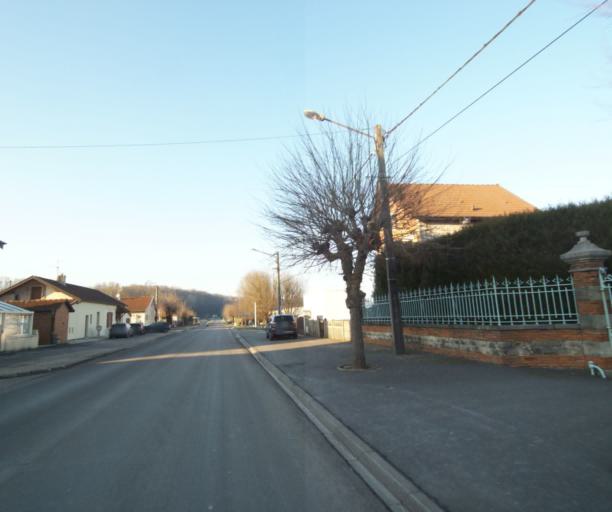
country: FR
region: Champagne-Ardenne
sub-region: Departement de la Haute-Marne
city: Bienville
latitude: 48.5883
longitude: 5.0350
